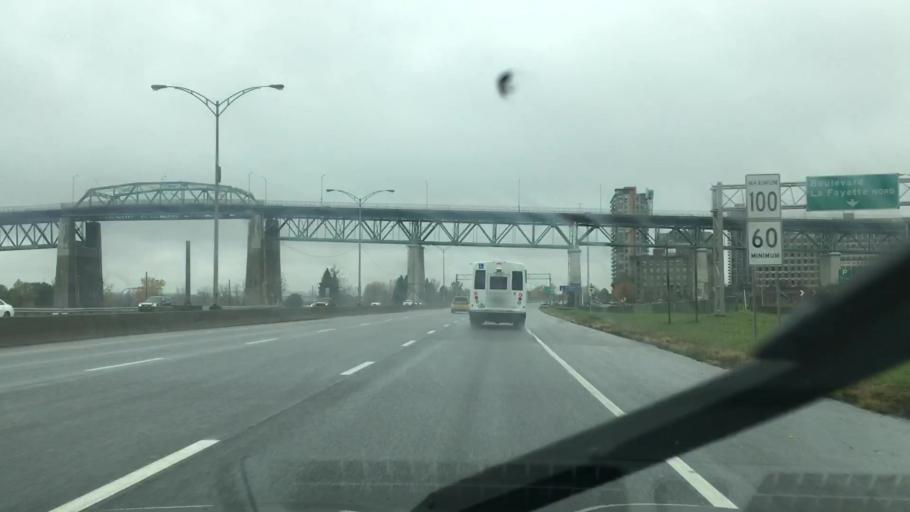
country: CA
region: Quebec
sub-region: Monteregie
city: Longueuil
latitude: 45.5186
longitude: -73.5233
